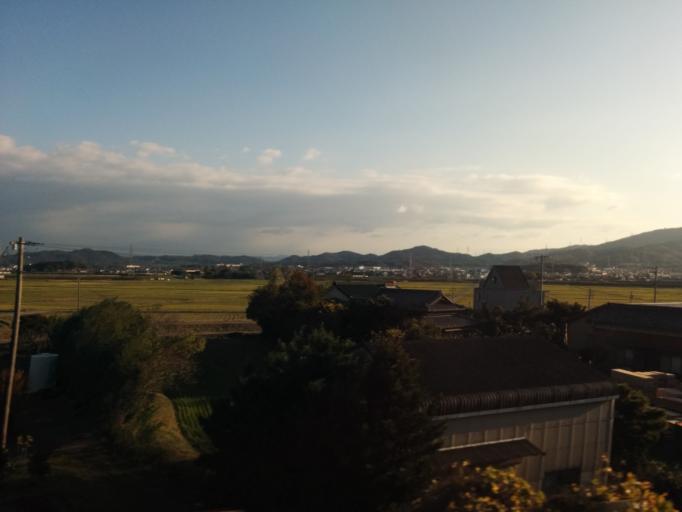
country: JP
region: Aichi
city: Okazaki
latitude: 34.8713
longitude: 137.1503
